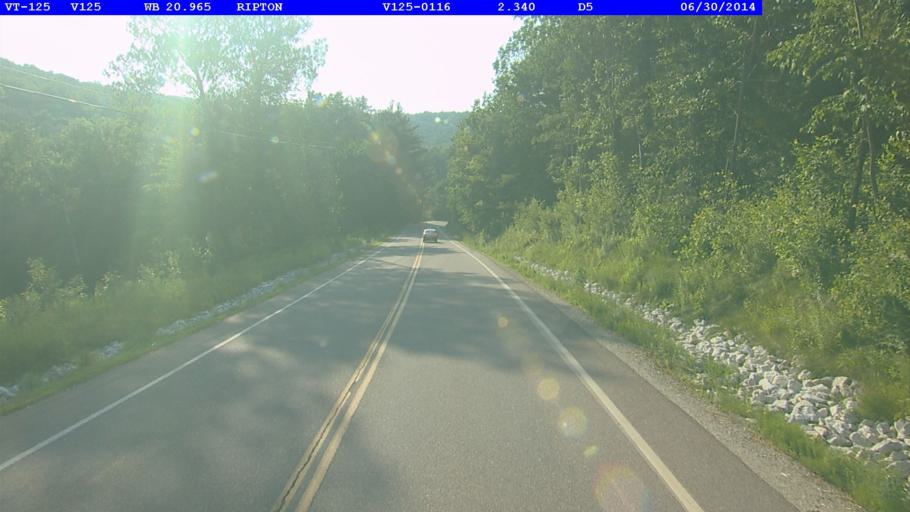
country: US
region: Vermont
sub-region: Addison County
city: Middlebury (village)
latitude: 43.9635
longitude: -73.0273
